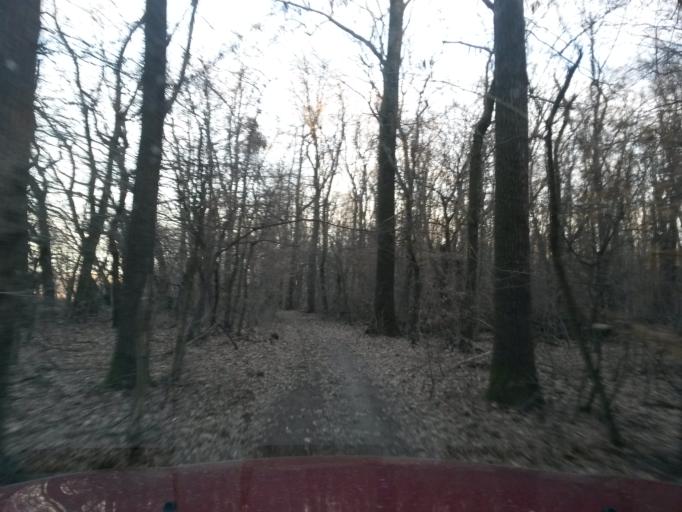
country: SK
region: Kosicky
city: Kosice
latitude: 48.7051
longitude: 21.3035
